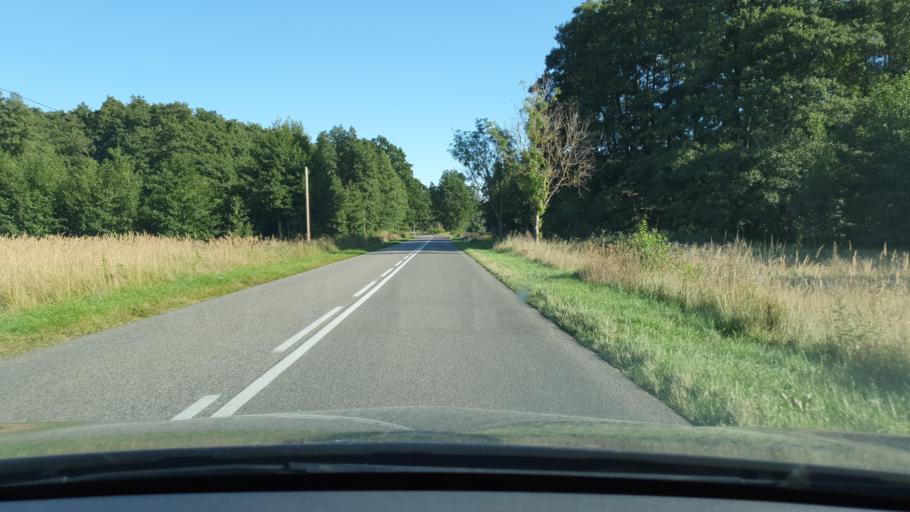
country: PL
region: West Pomeranian Voivodeship
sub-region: Powiat goleniowski
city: Przybiernow
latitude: 53.8297
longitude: 14.7765
